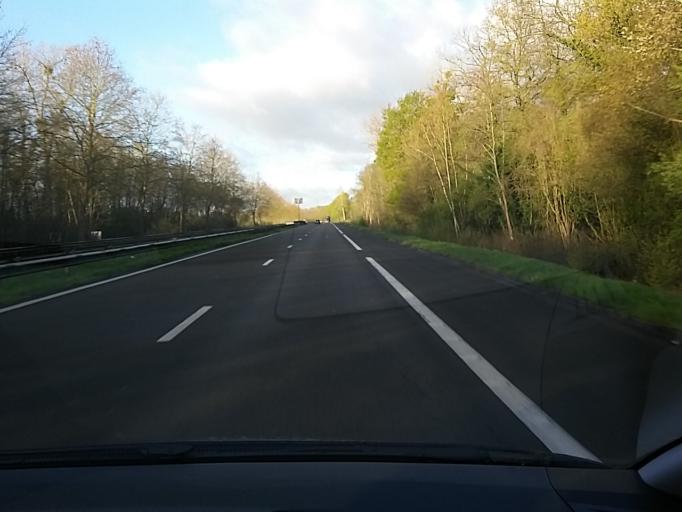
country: FR
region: Picardie
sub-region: Departement de l'Oise
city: Le Meux
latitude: 49.3521
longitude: 2.7501
